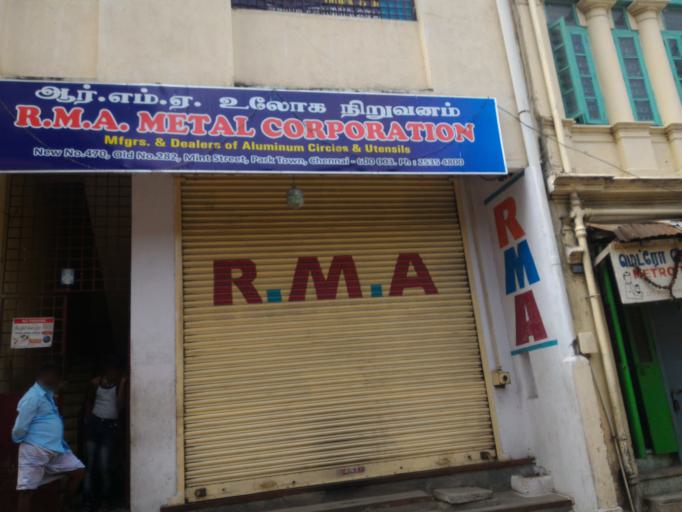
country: IN
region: Tamil Nadu
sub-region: Chennai
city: Chennai
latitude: 13.0857
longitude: 80.2783
